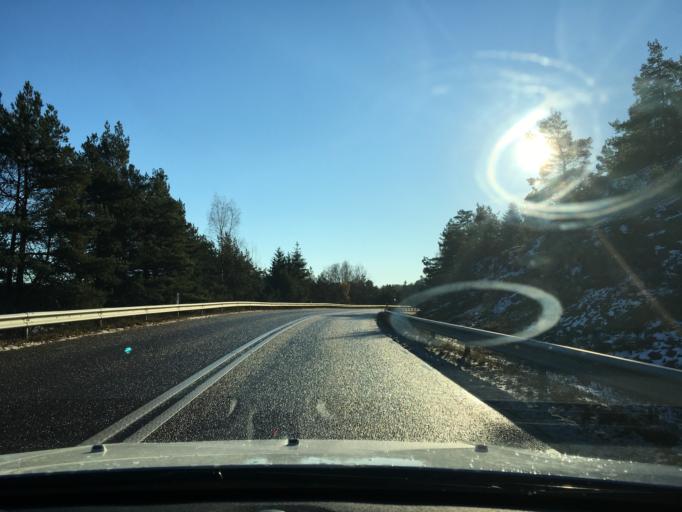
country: SE
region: Vaestra Goetaland
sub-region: Tjorns Kommun
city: Myggenas
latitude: 58.0743
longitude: 11.6964
